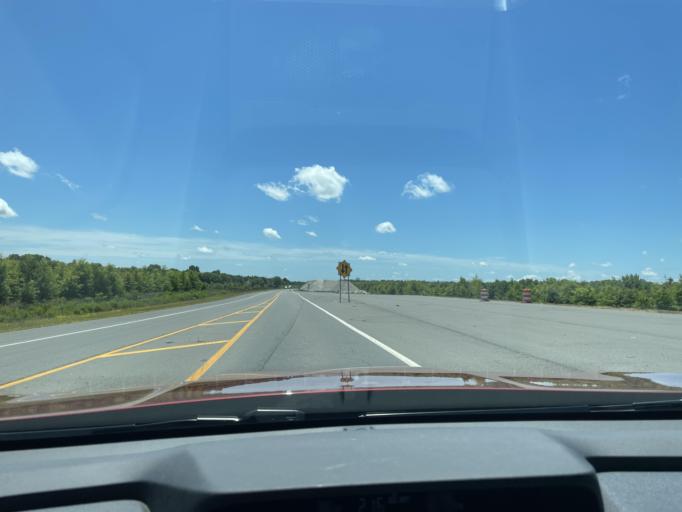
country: US
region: Arkansas
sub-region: Jefferson County
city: Pine Bluff
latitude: 34.1626
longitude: -91.9844
